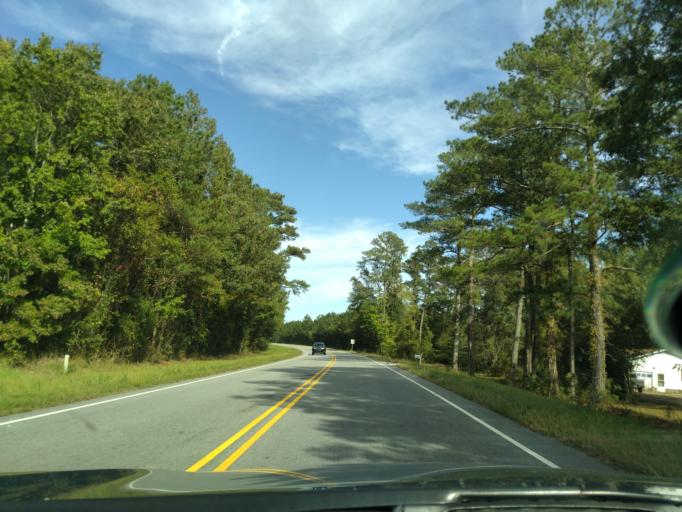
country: US
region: North Carolina
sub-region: Beaufort County
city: River Road
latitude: 35.5128
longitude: -76.9004
